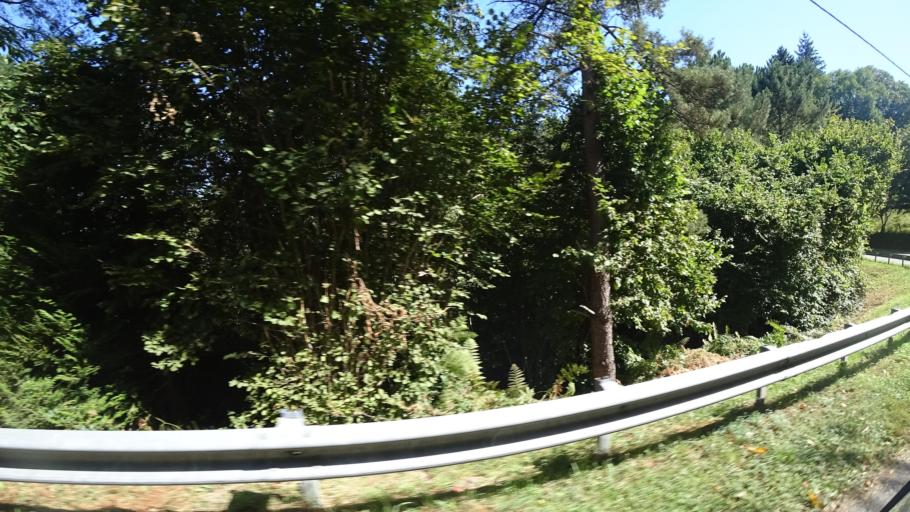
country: FR
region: Midi-Pyrenees
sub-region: Departement de l'Aveyron
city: Firmi
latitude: 44.5183
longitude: 2.3083
